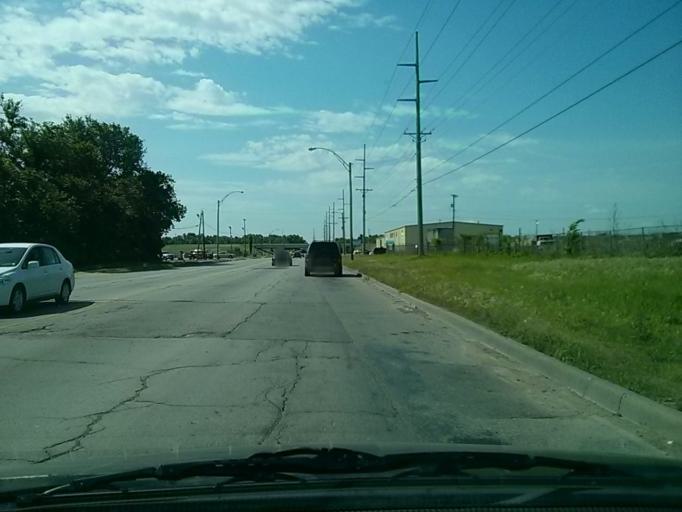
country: US
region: Oklahoma
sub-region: Tulsa County
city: Turley
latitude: 36.2014
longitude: -95.9756
